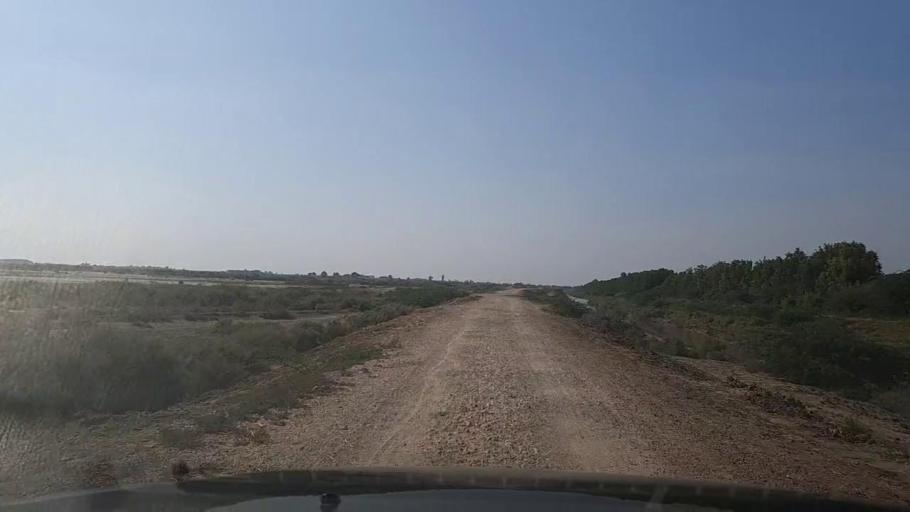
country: PK
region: Sindh
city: Thatta
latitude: 24.7111
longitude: 67.7608
